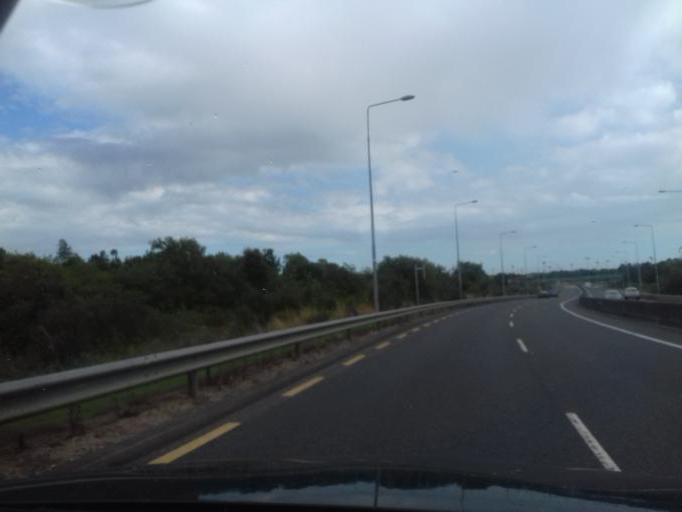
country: IE
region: Munster
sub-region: Waterford
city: Waterford
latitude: 52.2589
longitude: -7.1816
